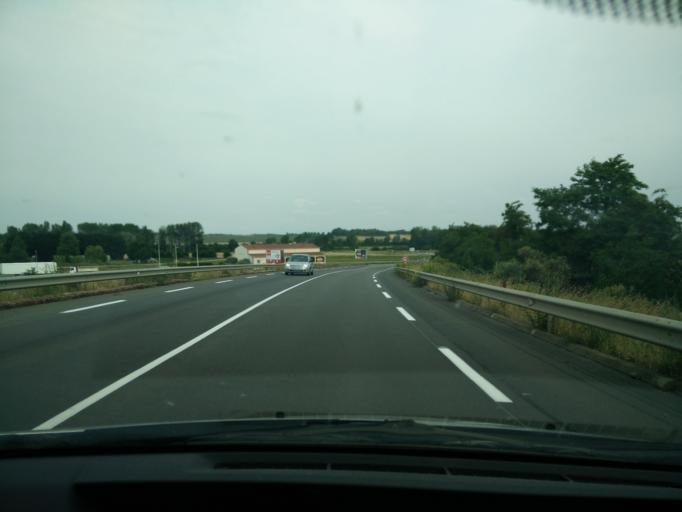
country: FR
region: Poitou-Charentes
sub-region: Departement des Deux-Sevres
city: Sainte-Verge
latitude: 47.0114
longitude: -0.1984
